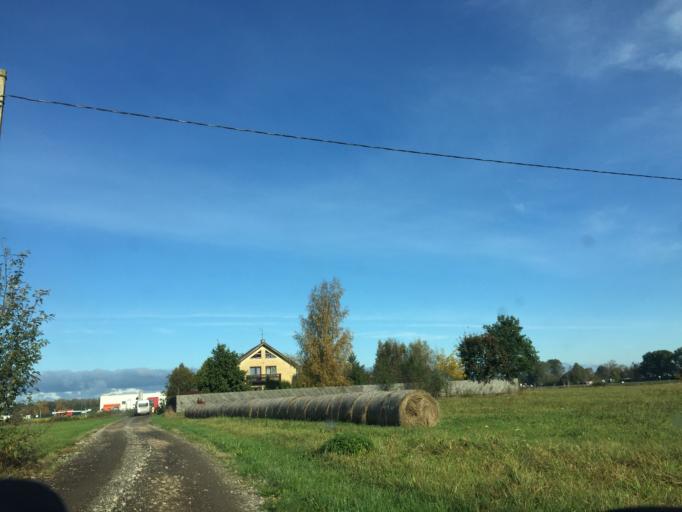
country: LV
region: Adazi
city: Adazi
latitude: 57.0929
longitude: 24.3080
